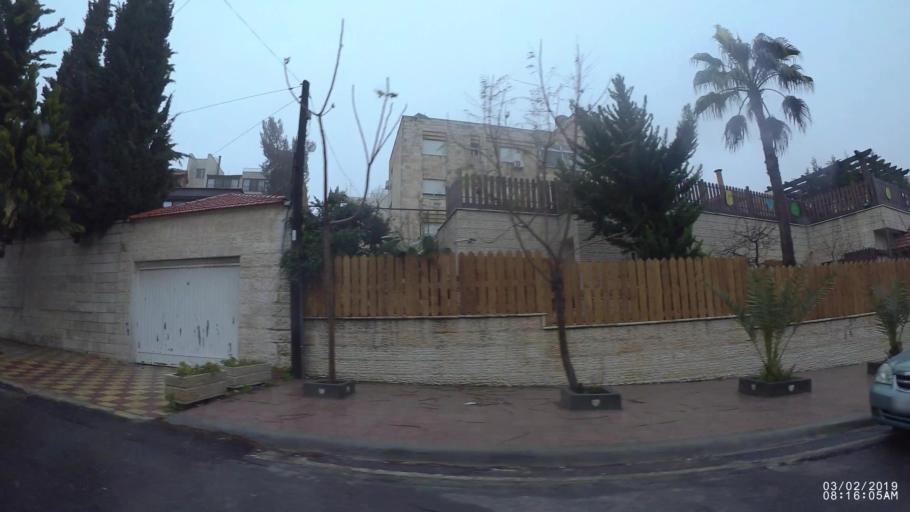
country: JO
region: Amman
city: Wadi as Sir
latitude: 31.9674
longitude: 35.8664
